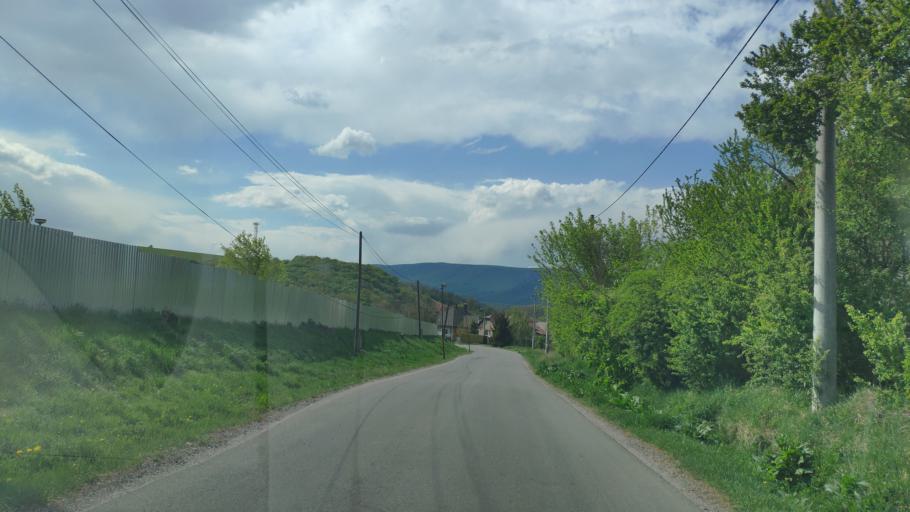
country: SK
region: Kosicky
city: Moldava nad Bodvou
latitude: 48.5851
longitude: 20.9201
